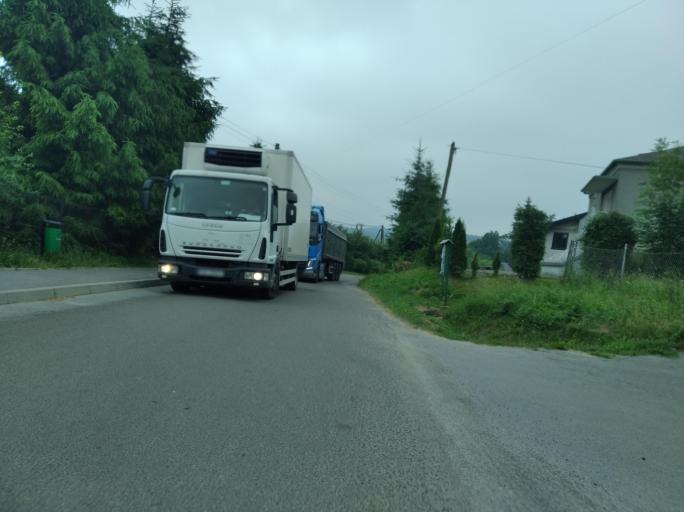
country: PL
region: Subcarpathian Voivodeship
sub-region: Powiat brzozowski
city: Jablonica Polska
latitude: 49.6994
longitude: 21.8972
